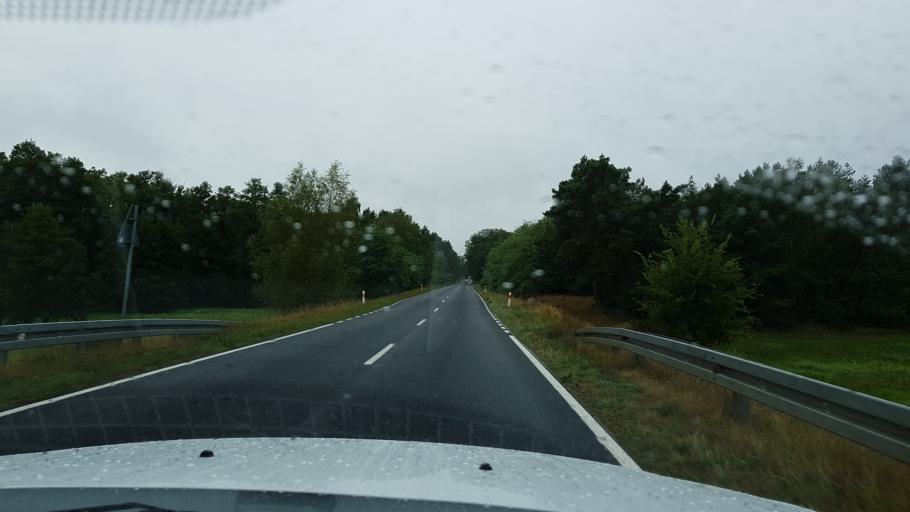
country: DE
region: Brandenburg
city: Schwedt (Oder)
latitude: 53.0581
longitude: 14.3573
